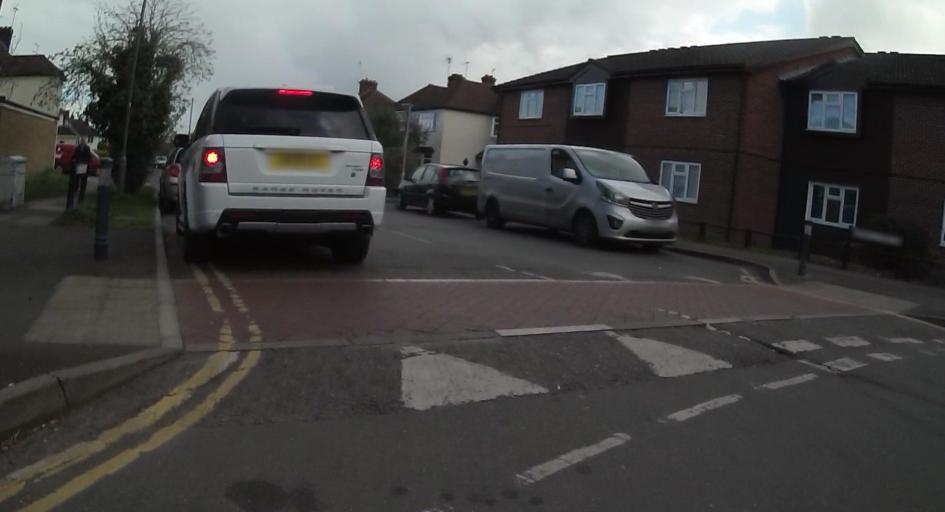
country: GB
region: England
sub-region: Surrey
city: West Byfleet
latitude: 51.3485
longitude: -0.5033
